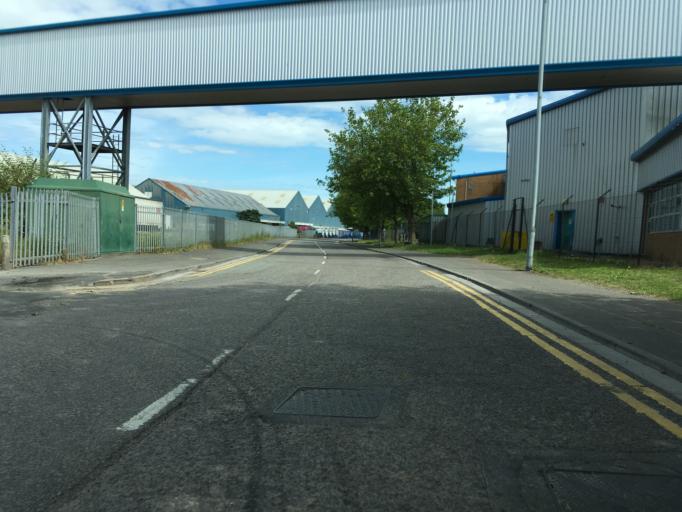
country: GB
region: Wales
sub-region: Newport
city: Nash
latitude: 51.5682
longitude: -2.9651
